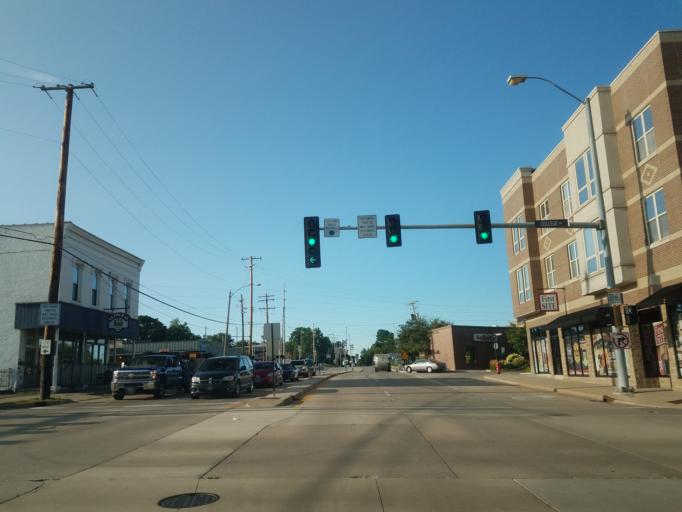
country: US
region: Illinois
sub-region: McLean County
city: Normal
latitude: 40.5105
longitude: -88.9825
